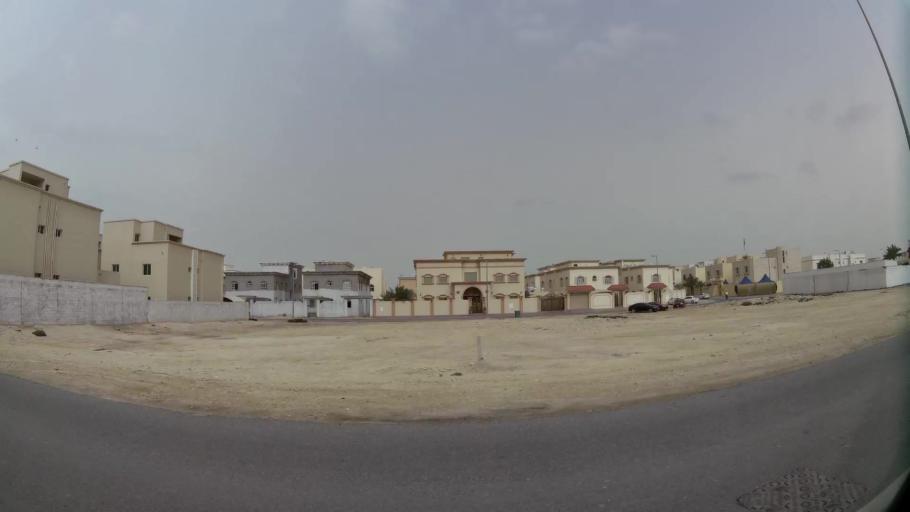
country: QA
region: Baladiyat ad Dawhah
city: Doha
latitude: 25.2425
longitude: 51.5377
